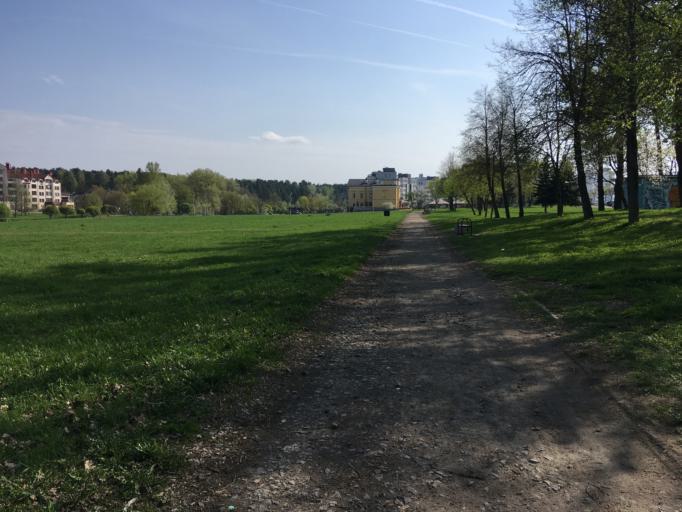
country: BY
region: Minsk
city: Minsk
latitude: 53.9220
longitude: 27.6394
